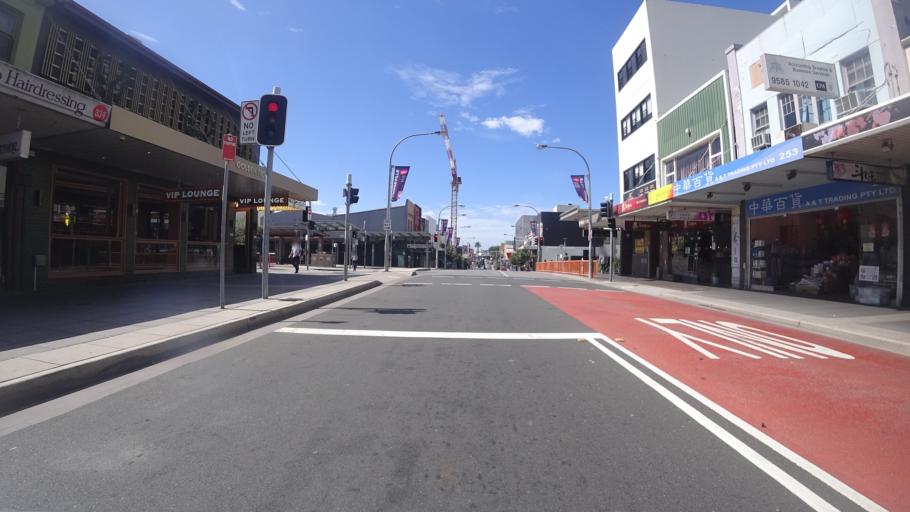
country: AU
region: New South Wales
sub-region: Hurstville
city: Earlwood
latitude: -33.9663
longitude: 151.1017
